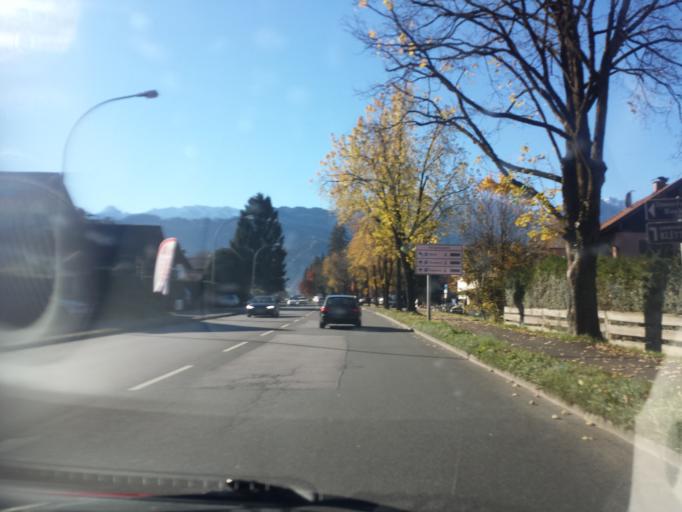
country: DE
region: Bavaria
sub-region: Upper Bavaria
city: Garmisch-Partenkirchen
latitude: 47.5065
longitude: 11.1041
